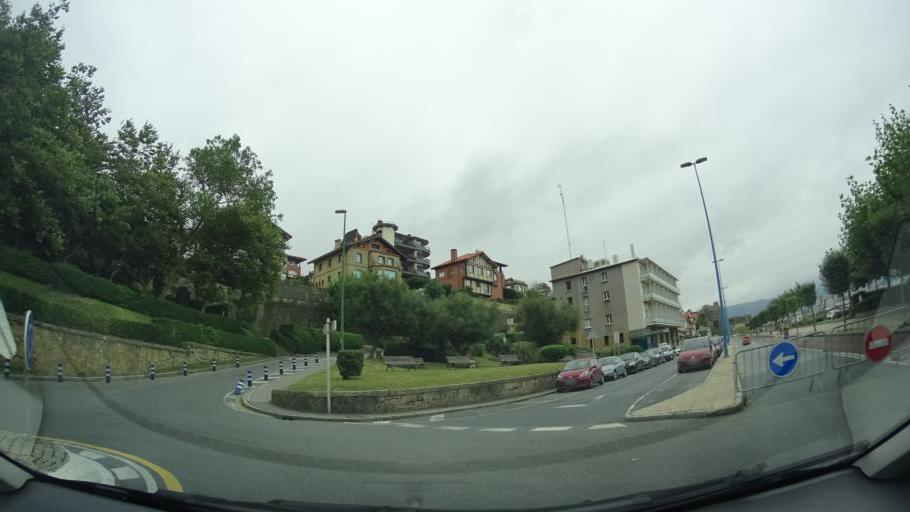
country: ES
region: Basque Country
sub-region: Bizkaia
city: Algorta
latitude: 43.3441
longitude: -3.0114
